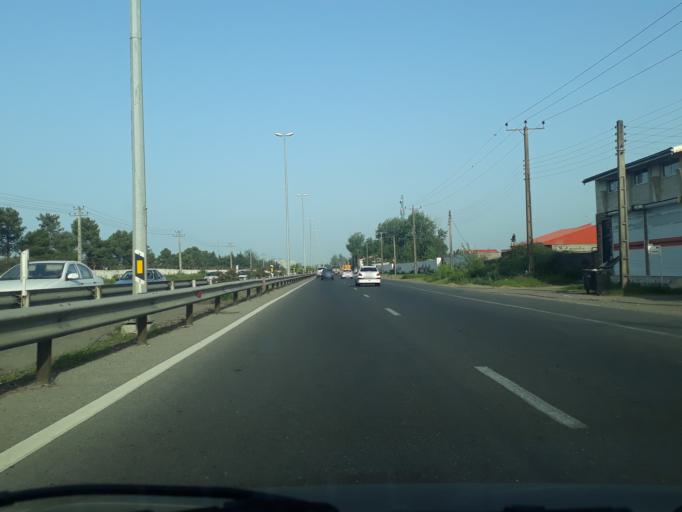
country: IR
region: Gilan
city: Bandar-e Anzali
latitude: 37.4584
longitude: 49.6023
